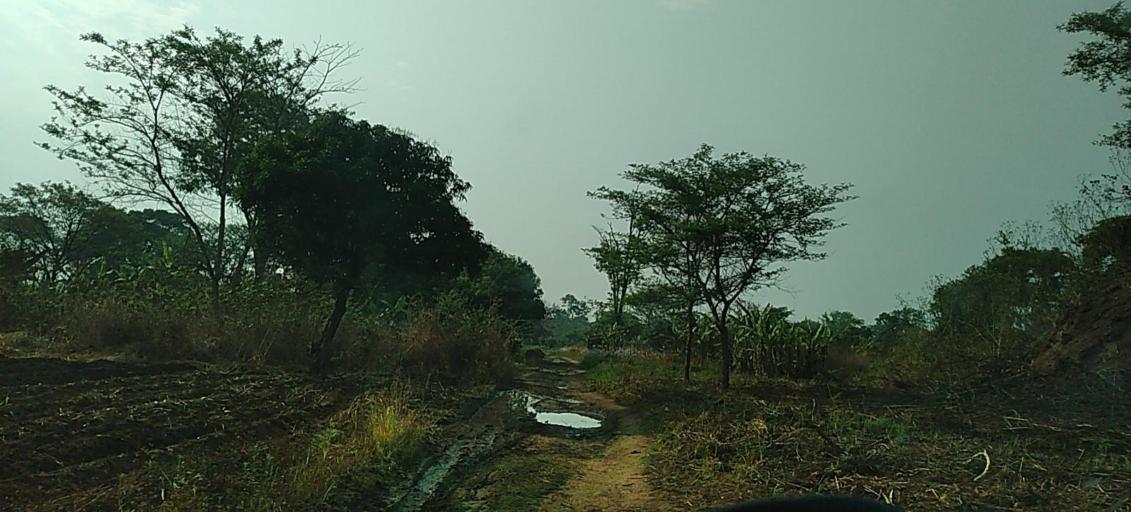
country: ZM
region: North-Western
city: Solwezi
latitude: -12.3848
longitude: 26.5669
